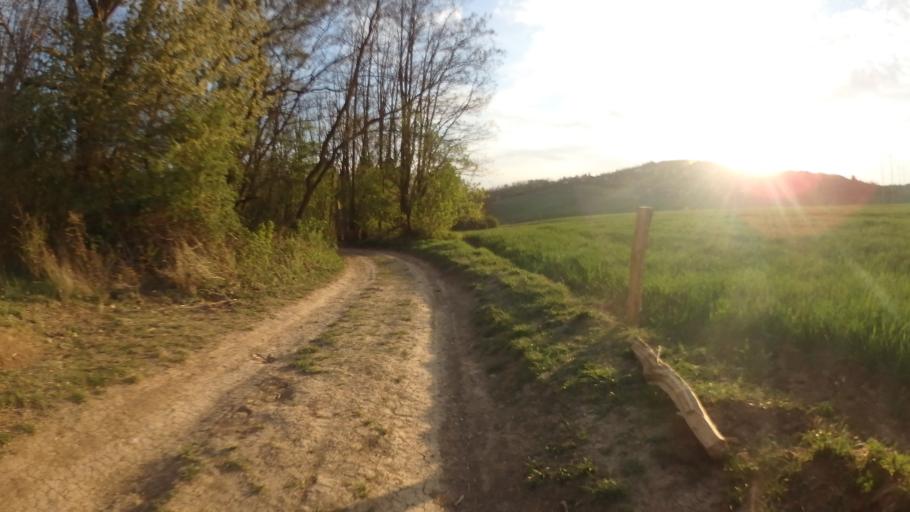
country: CZ
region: South Moravian
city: Moravany
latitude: 49.1350
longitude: 16.5595
